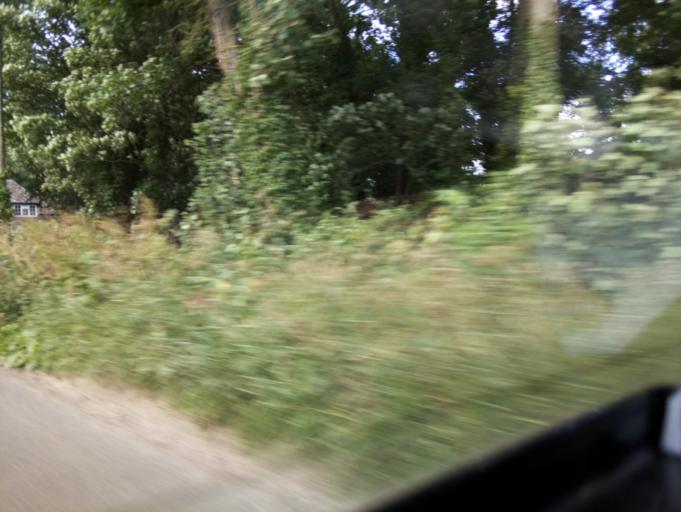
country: GB
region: England
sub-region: Gloucestershire
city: Donnington
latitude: 51.9802
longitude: -1.7552
